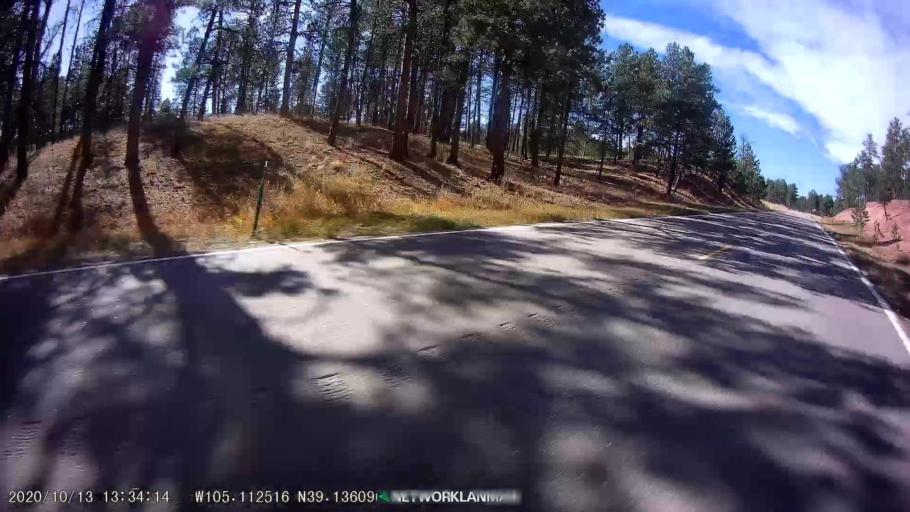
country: US
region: Colorado
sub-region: Teller County
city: Woodland Park
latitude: 39.1363
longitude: -105.1128
